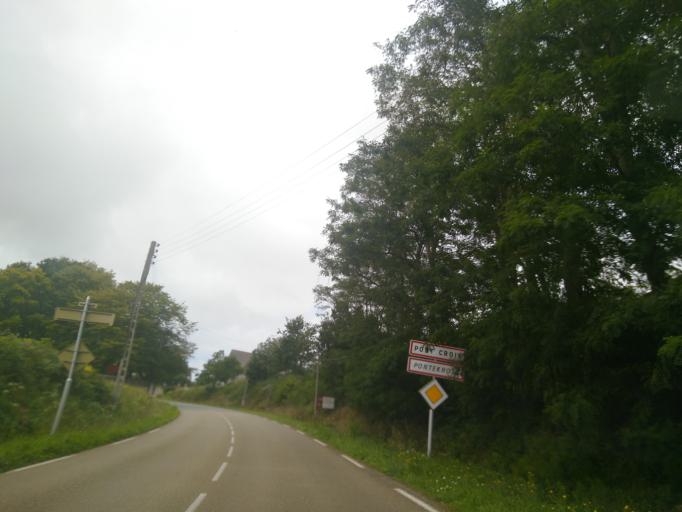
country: FR
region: Brittany
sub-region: Departement du Finistere
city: Plouhinec
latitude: 48.0439
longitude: -4.4835
